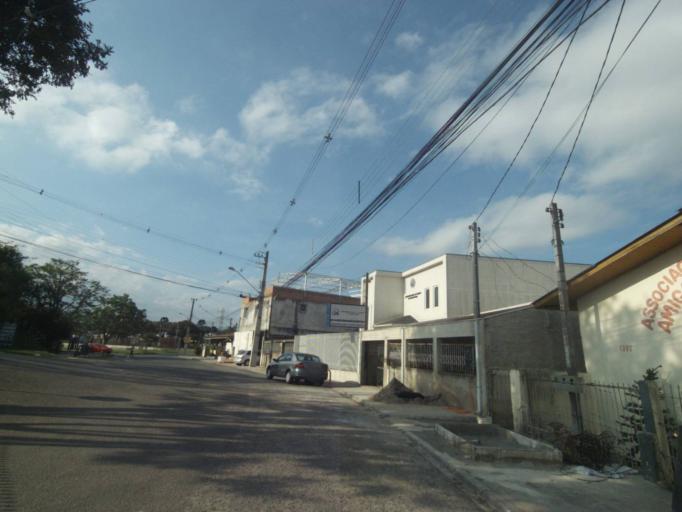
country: BR
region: Parana
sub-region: Pinhais
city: Pinhais
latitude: -25.4053
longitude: -49.1952
